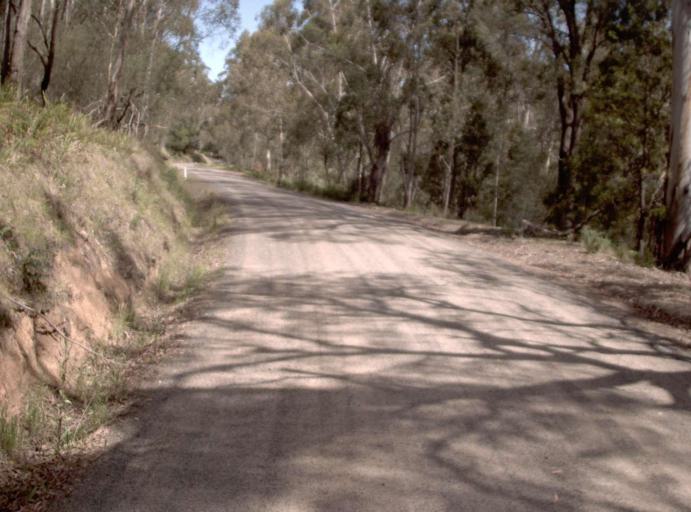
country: AU
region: New South Wales
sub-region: Bombala
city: Bombala
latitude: -37.1617
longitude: 148.6759
